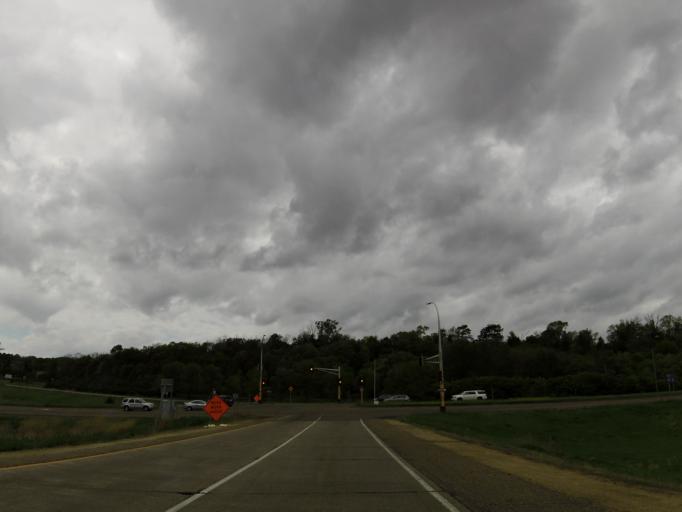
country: US
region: Minnesota
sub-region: Washington County
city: Lakeland
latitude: 44.9629
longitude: -92.7723
